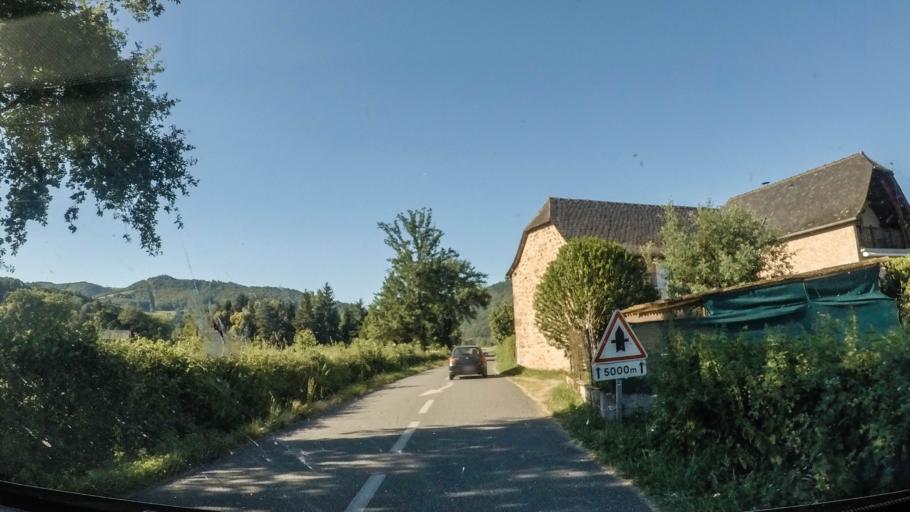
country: FR
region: Midi-Pyrenees
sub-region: Departement de l'Aveyron
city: Saint-Christophe-Vallon
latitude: 44.5479
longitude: 2.4045
